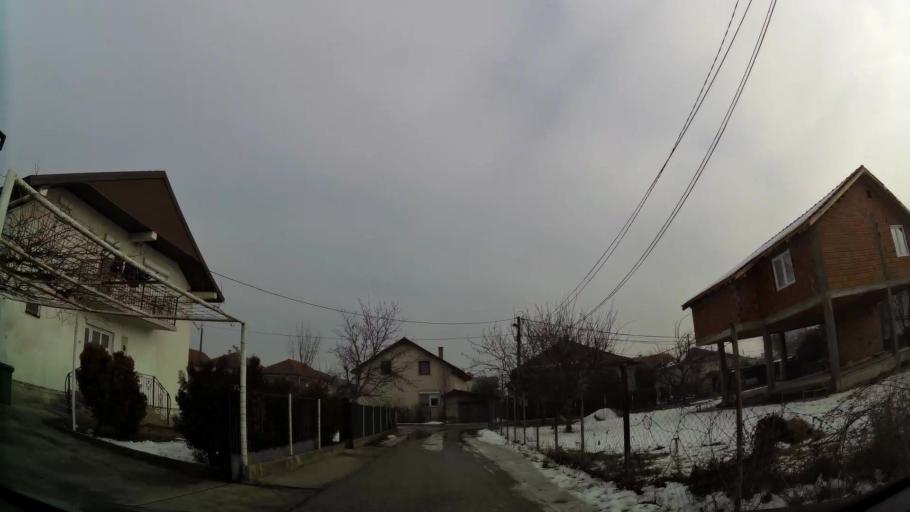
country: MK
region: Ilinden
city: Ilinden
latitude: 41.9927
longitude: 21.5834
